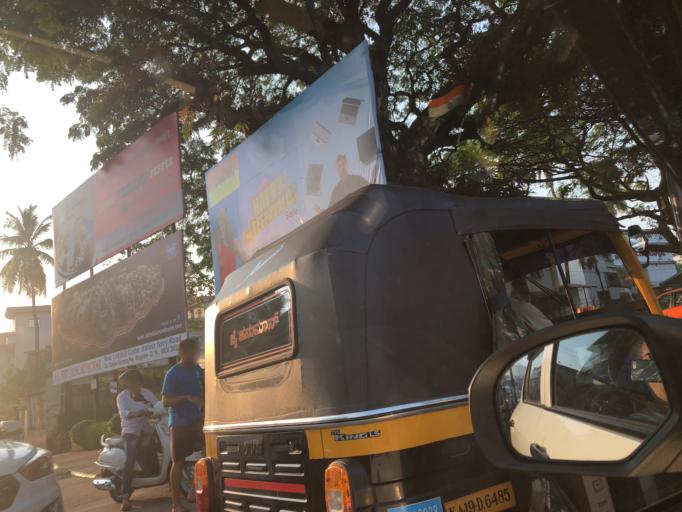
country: IN
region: Karnataka
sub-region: Dakshina Kannada
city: Mangalore
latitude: 12.8825
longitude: 74.8393
